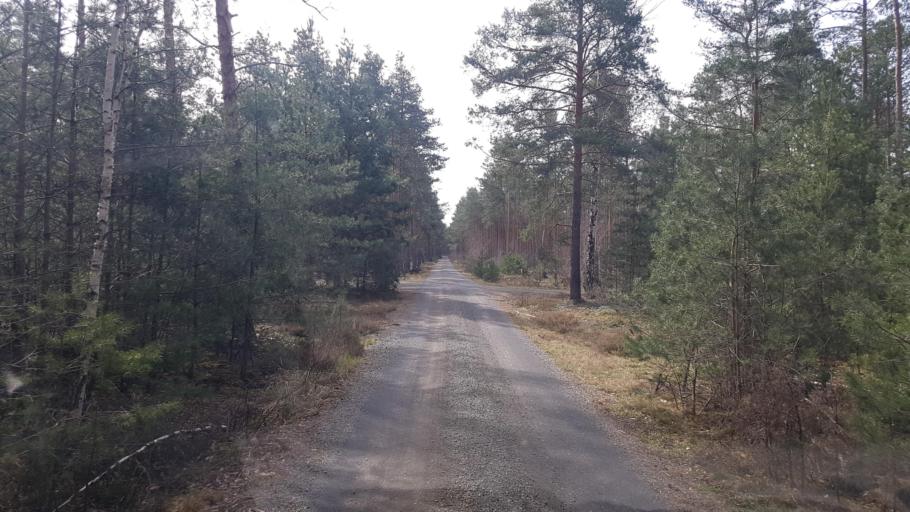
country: DE
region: Brandenburg
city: Bad Liebenwerda
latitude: 51.5004
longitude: 13.4564
